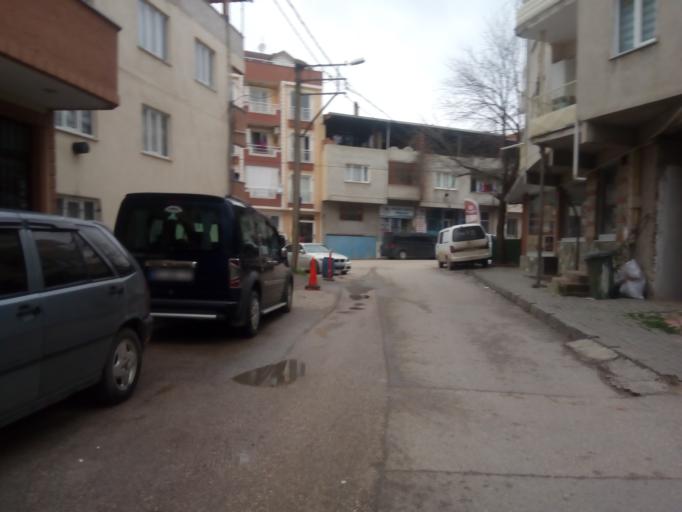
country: TR
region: Bursa
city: Niluefer
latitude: 40.2555
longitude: 28.9618
